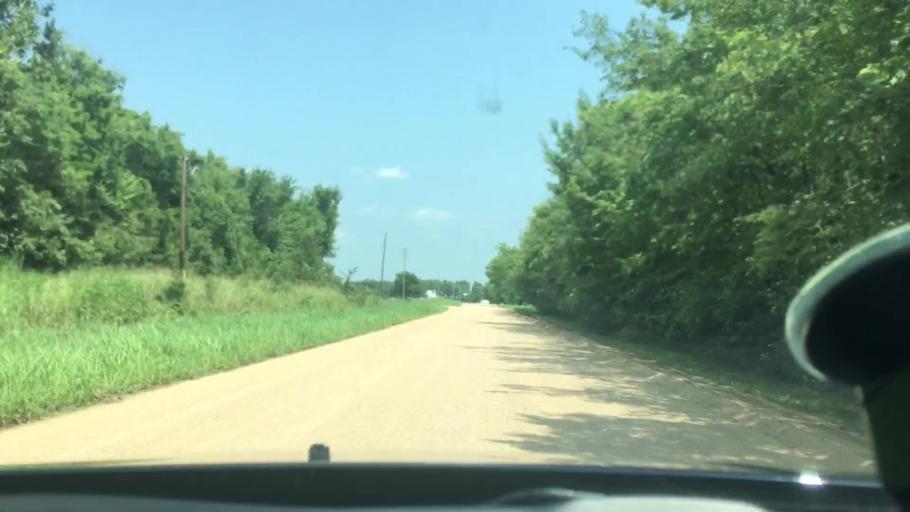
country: US
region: Oklahoma
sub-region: Coal County
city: Coalgate
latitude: 34.4330
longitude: -96.4436
